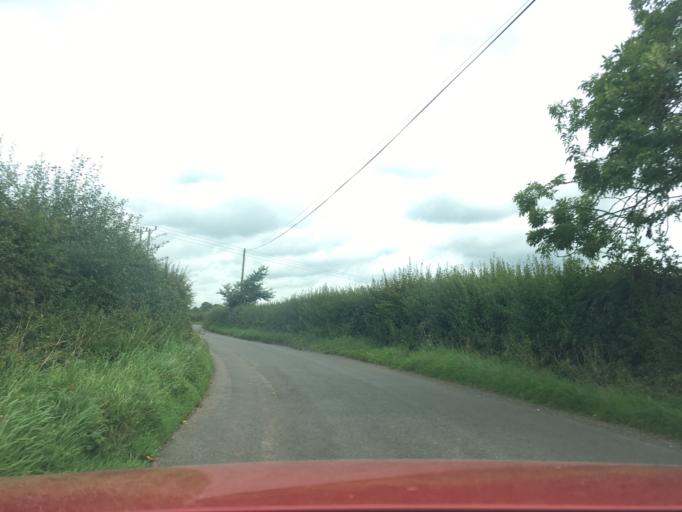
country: GB
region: England
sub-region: South Gloucestershire
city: Tytherington
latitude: 51.5864
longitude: -2.4841
